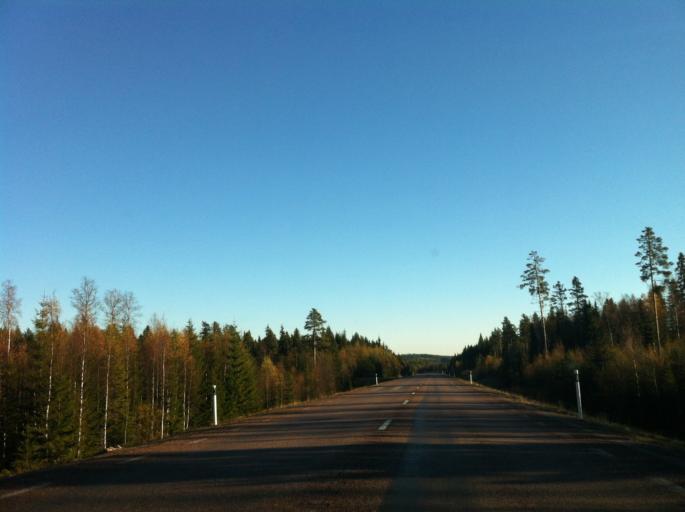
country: SE
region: Dalarna
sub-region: Rattviks Kommun
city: Raettvik
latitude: 60.8302
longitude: 15.2406
